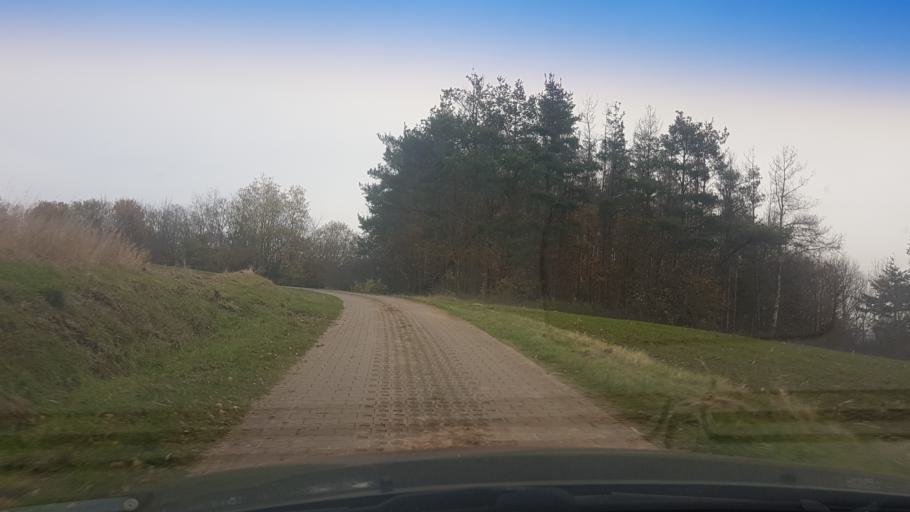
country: DE
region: Bavaria
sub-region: Upper Franconia
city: Baunach
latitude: 49.9957
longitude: 10.8634
